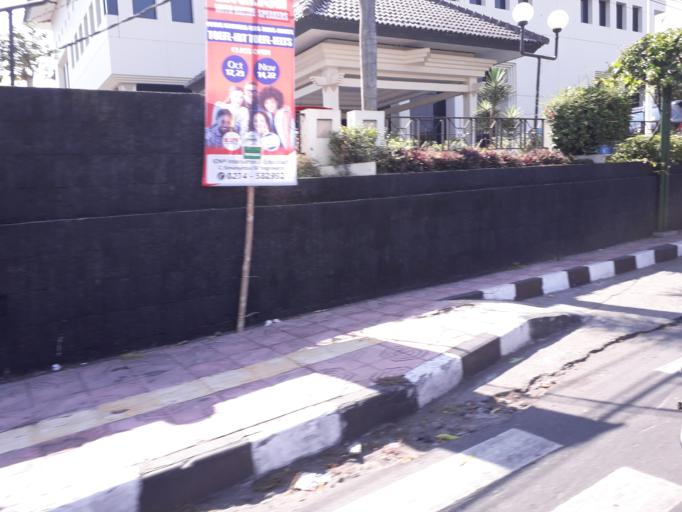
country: ID
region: Daerah Istimewa Yogyakarta
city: Yogyakarta
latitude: -7.7818
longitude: 110.3752
